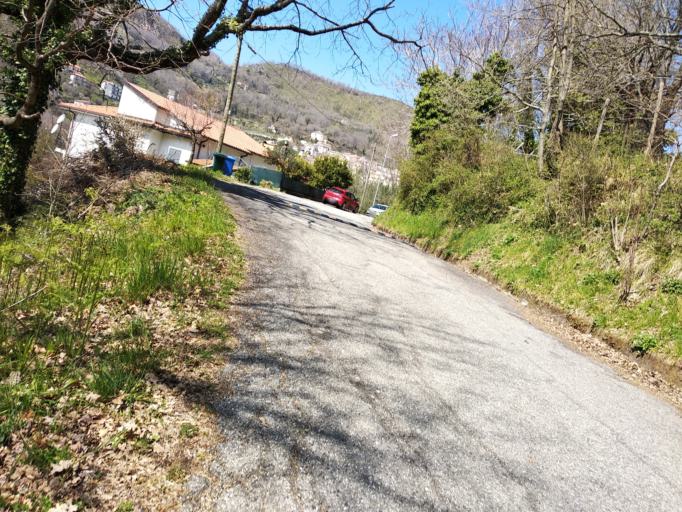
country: IT
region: Calabria
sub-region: Provincia di Cosenza
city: Altilia
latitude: 39.1284
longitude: 16.2474
